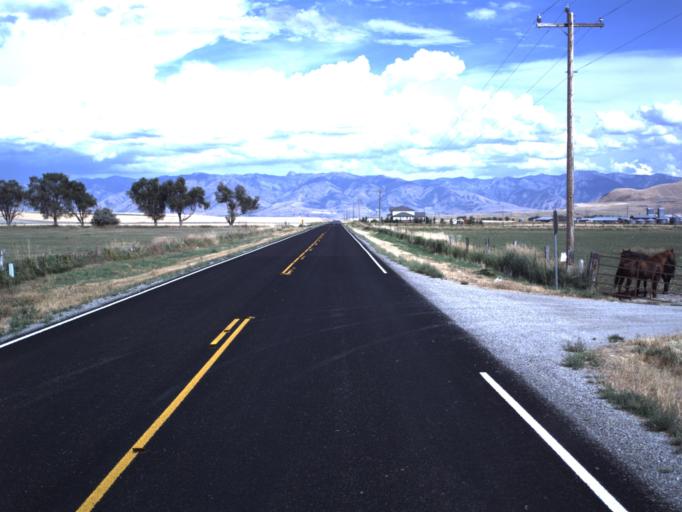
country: US
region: Utah
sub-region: Cache County
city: Benson
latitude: 41.9196
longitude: -112.0294
